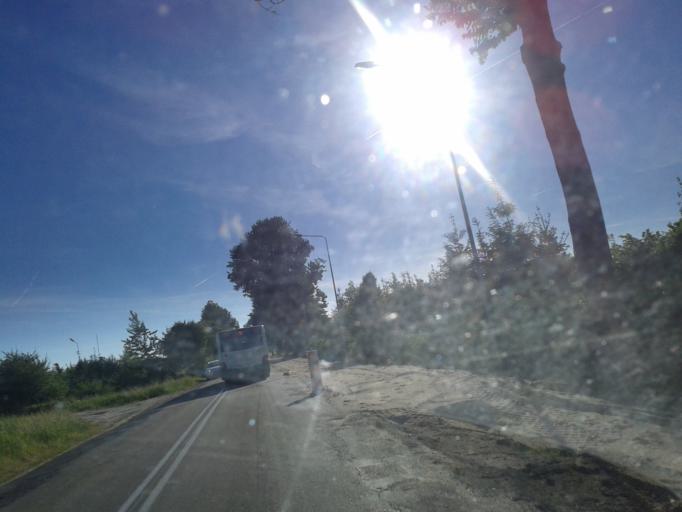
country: PL
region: West Pomeranian Voivodeship
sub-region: Powiat szczecinecki
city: Szczecinek
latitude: 53.7177
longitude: 16.6284
